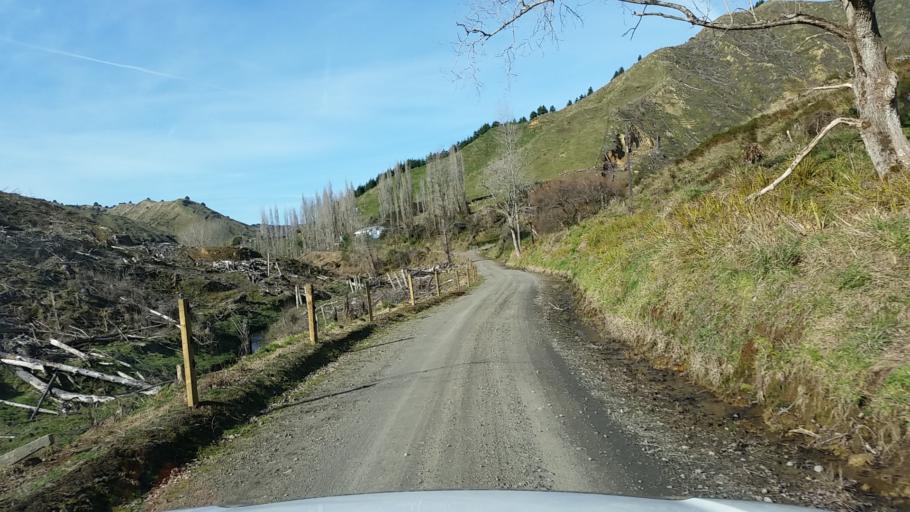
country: NZ
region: Taranaki
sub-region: South Taranaki District
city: Eltham
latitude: -39.3639
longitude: 174.5164
